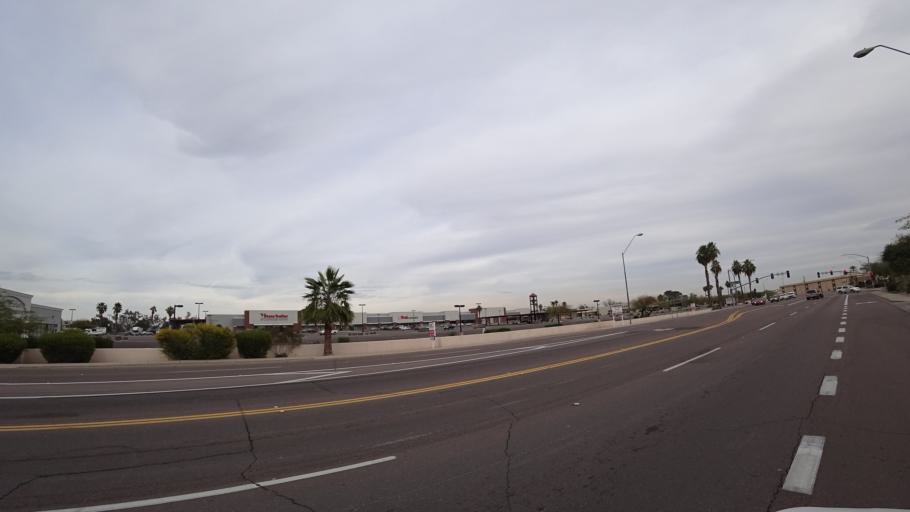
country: US
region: Arizona
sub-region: Maricopa County
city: Peoria
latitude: 33.5826
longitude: -112.2370
